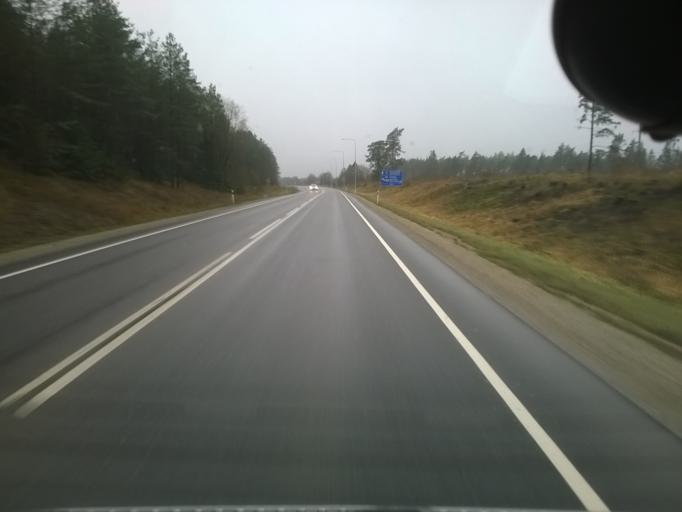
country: EE
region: Laeaene
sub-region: Lihula vald
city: Lihula
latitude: 58.9734
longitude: 23.9079
